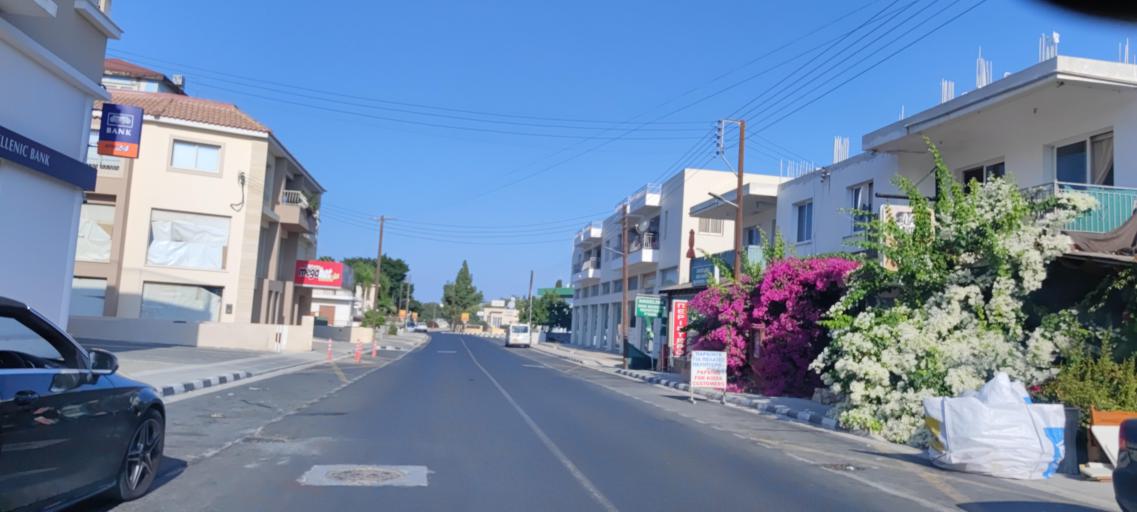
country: CY
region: Pafos
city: Chlorakas
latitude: 34.7933
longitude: 32.4149
